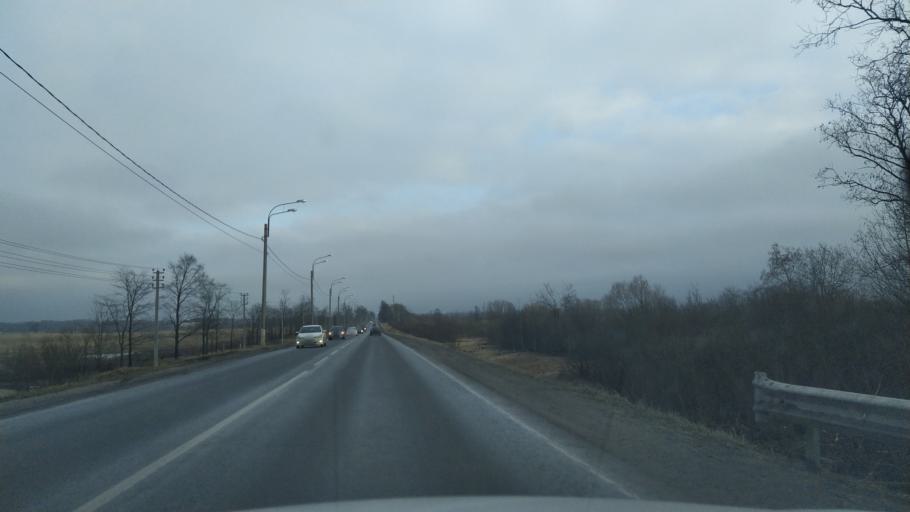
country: RU
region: St.-Petersburg
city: Aleksandrovskaya
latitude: 59.7120
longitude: 30.3114
